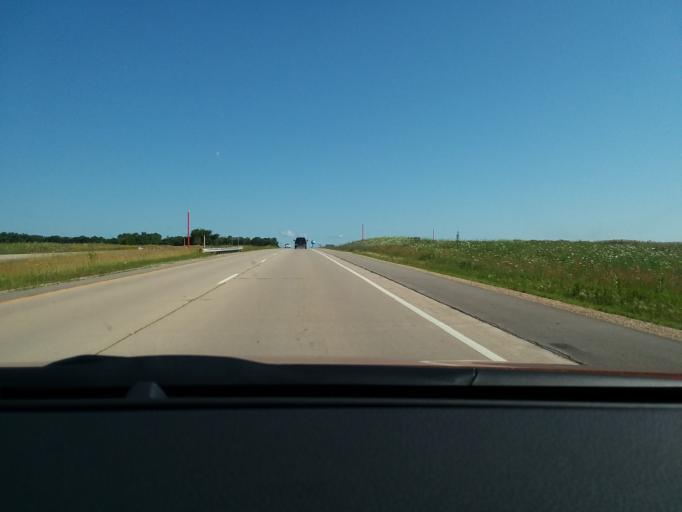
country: US
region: Wisconsin
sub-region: Dane County
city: Windsor
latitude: 43.1551
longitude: -89.3247
